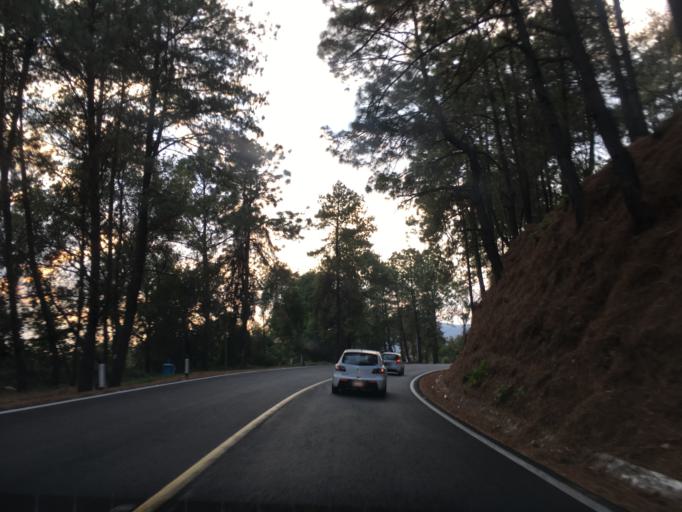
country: MX
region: Michoacan
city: Tingambato
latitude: 19.4940
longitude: -101.8332
